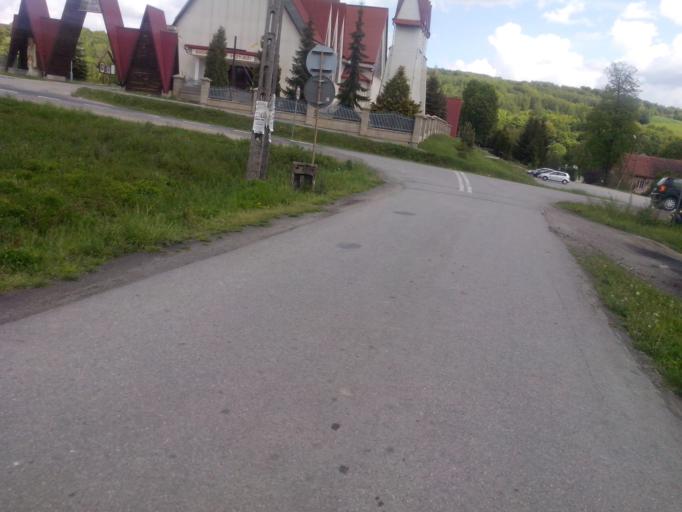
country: PL
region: Subcarpathian Voivodeship
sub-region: Powiat strzyzowski
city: Strzyzow
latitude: 49.8444
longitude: 21.8113
